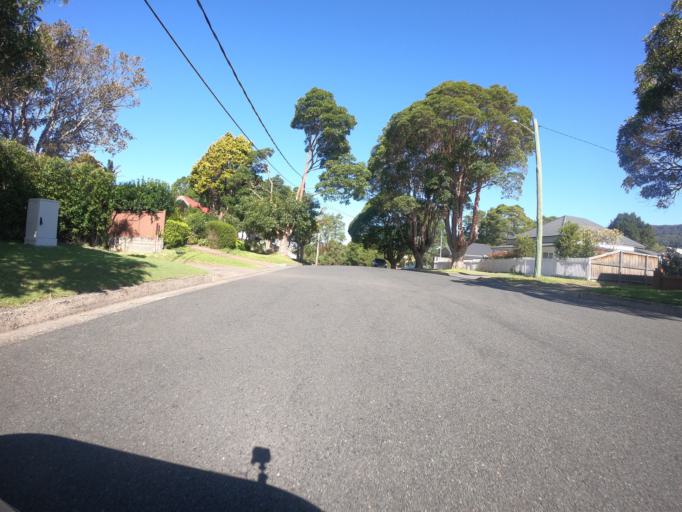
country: AU
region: New South Wales
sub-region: Wollongong
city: Bulli
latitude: -34.3475
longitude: 150.9078
